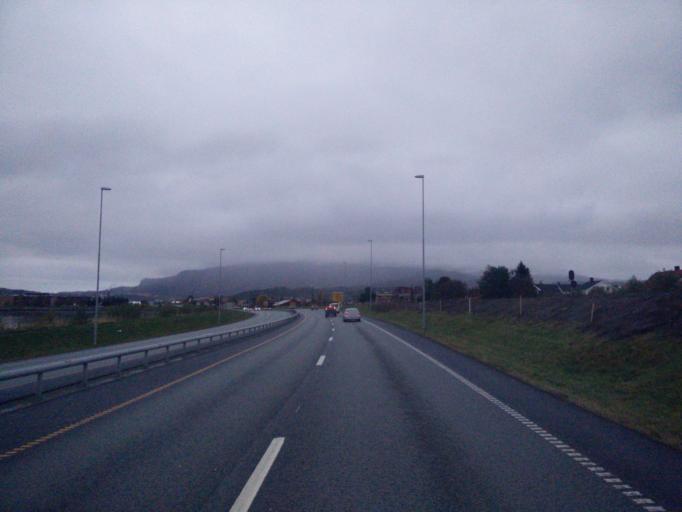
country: NO
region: Nord-Trondelag
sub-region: Stjordal
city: Stjordal
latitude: 63.4631
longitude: 10.9129
